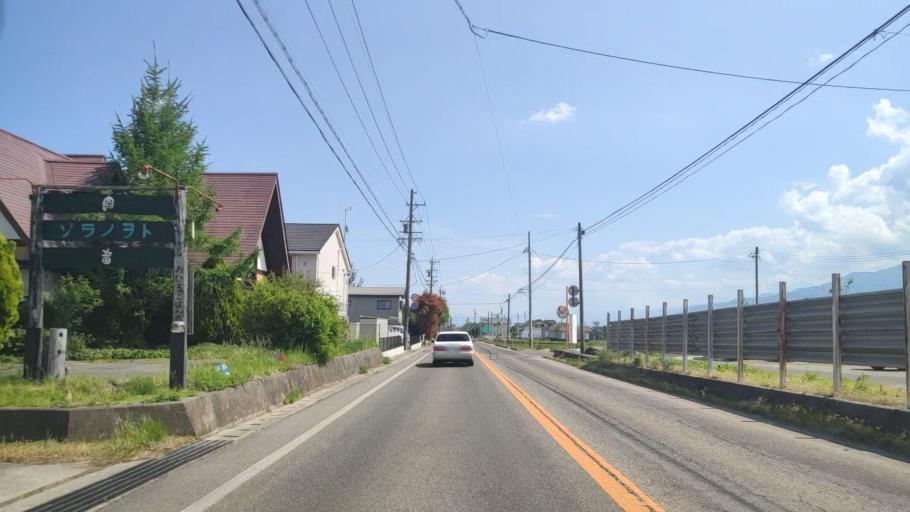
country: JP
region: Nagano
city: Hotaka
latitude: 36.3927
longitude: 137.8638
